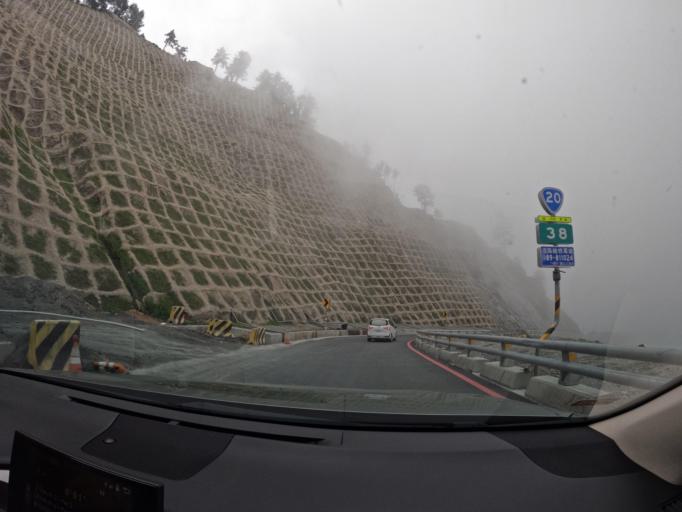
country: TW
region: Taiwan
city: Lugu
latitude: 23.2673
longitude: 120.9682
